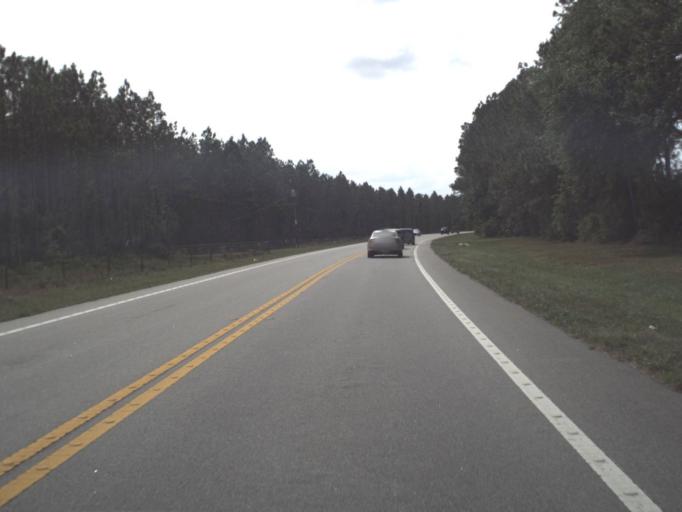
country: US
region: Florida
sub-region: Putnam County
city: Crescent City
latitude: 29.4808
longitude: -81.4495
